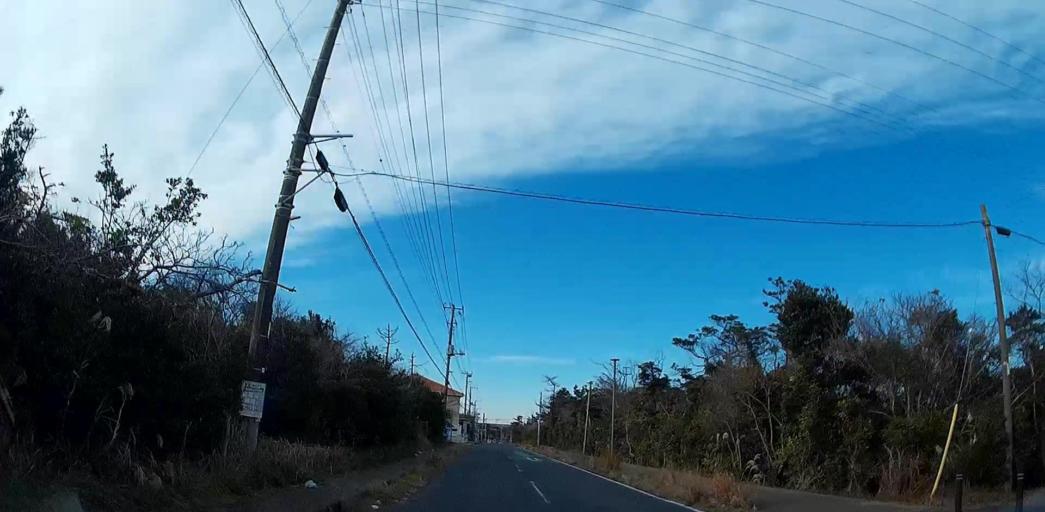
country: JP
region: Chiba
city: Hasaki
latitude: 35.7494
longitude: 140.8318
